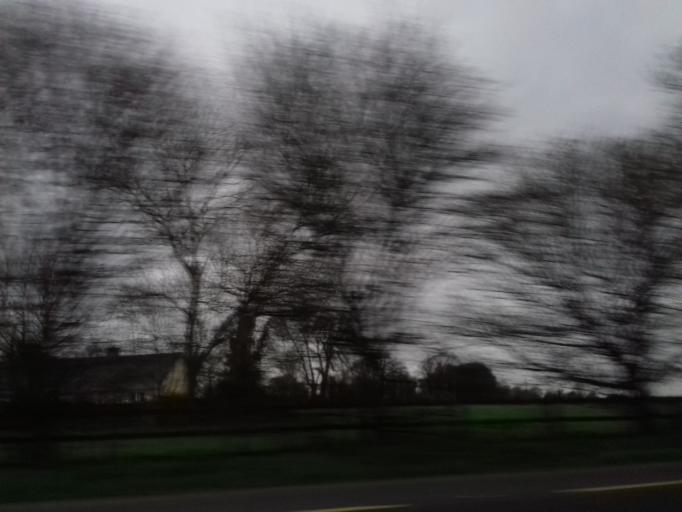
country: IE
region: Munster
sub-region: County Limerick
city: Adare
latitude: 52.5412
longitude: -8.8582
